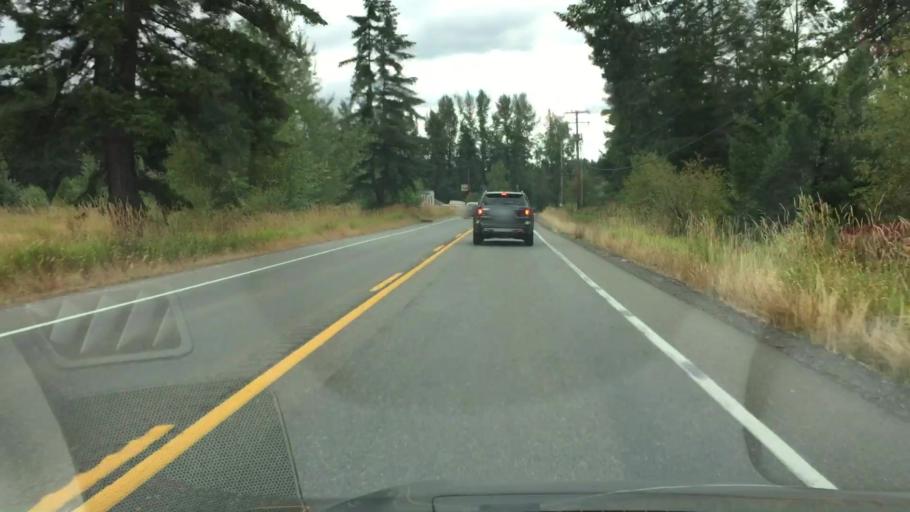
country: US
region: Washington
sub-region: Pierce County
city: Graham
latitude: 46.9962
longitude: -122.2957
